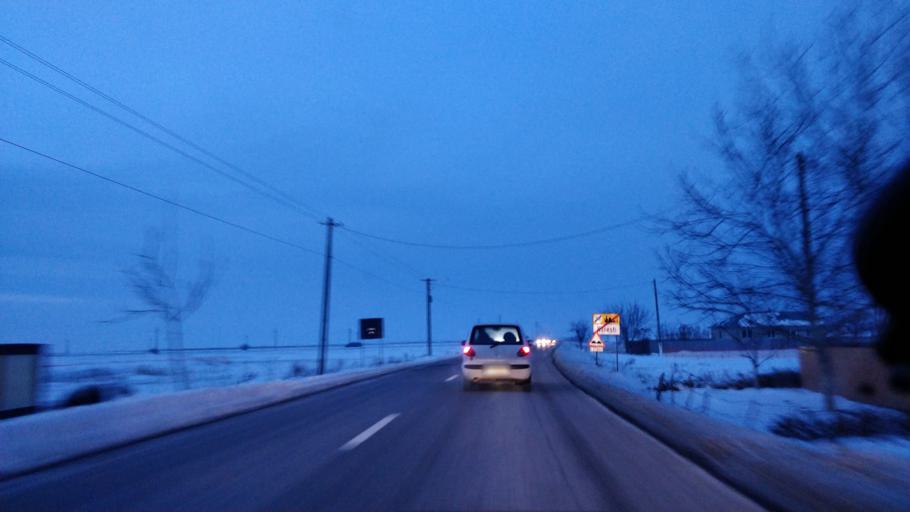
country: RO
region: Vrancea
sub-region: Comuna Nanesti
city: Nanesti
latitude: 45.5545
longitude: 27.5001
